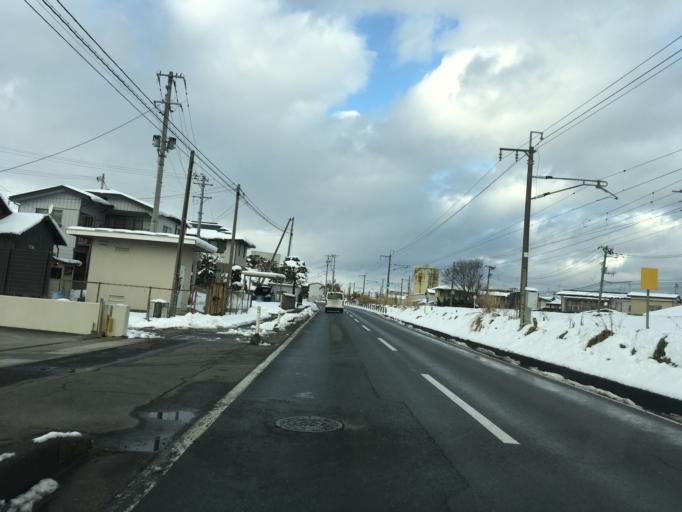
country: JP
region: Iwate
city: Mizusawa
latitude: 39.1319
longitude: 141.1464
